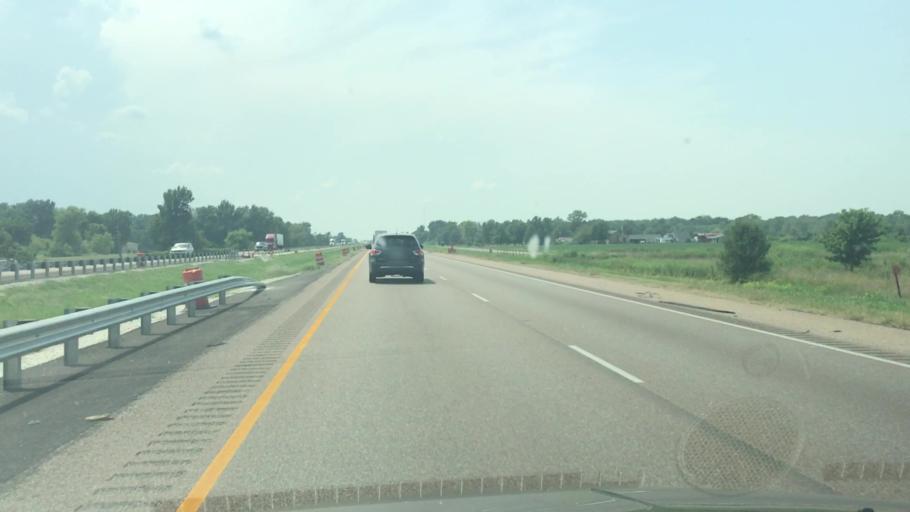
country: US
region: Arkansas
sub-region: Crittenden County
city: Earle
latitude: 35.1500
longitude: -90.3639
